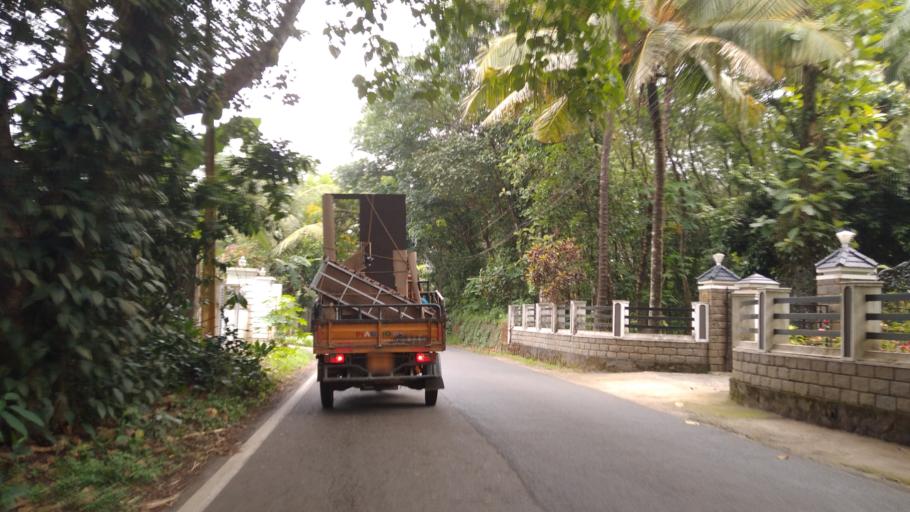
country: IN
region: Kerala
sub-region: Ernakulam
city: Ramamangalam
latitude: 10.0113
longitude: 76.4846
